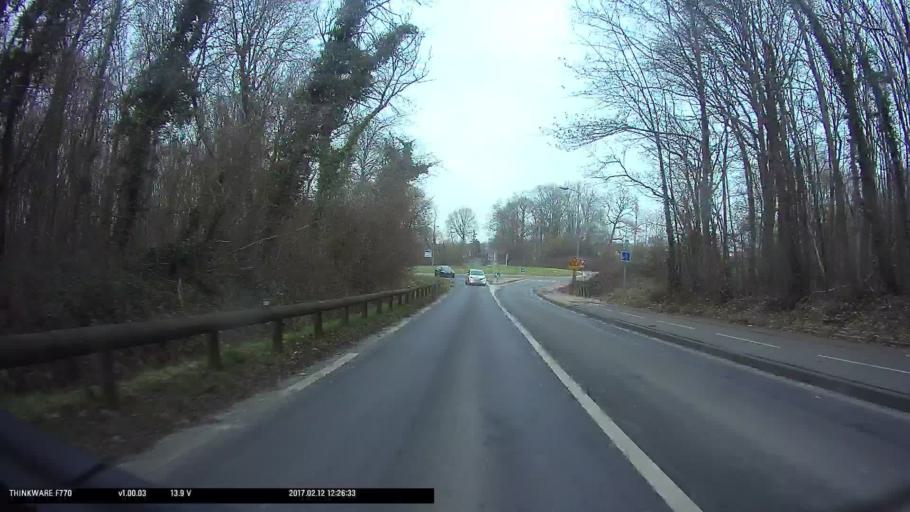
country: FR
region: Ile-de-France
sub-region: Departement du Val-d'Oise
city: Courdimanche
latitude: 49.0284
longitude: 1.9990
